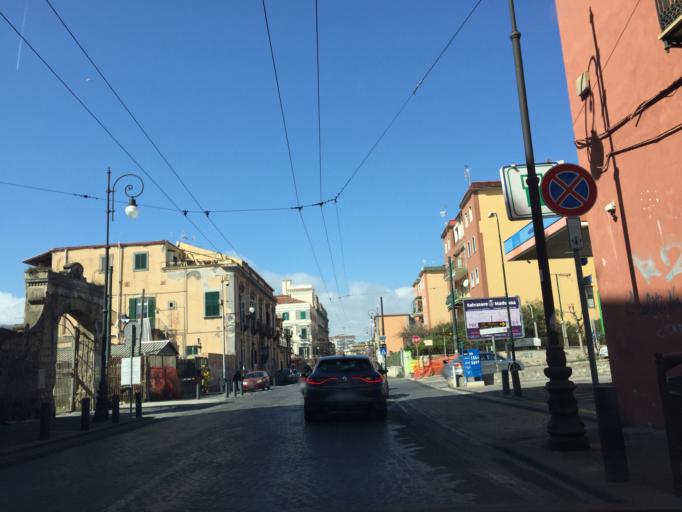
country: IT
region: Campania
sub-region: Provincia di Napoli
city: Portici
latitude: 40.8217
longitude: 14.3249
